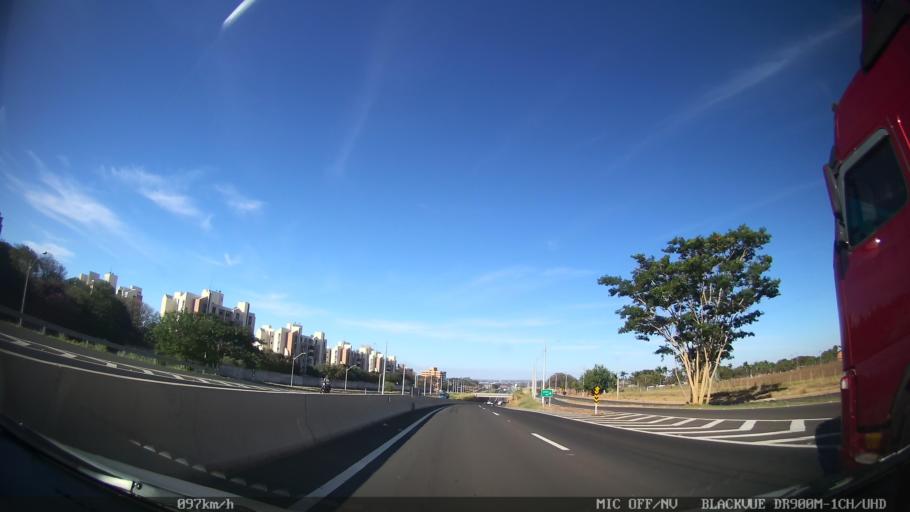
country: BR
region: Sao Paulo
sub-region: Sao Jose Do Rio Preto
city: Sao Jose do Rio Preto
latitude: -20.8513
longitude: -49.3962
